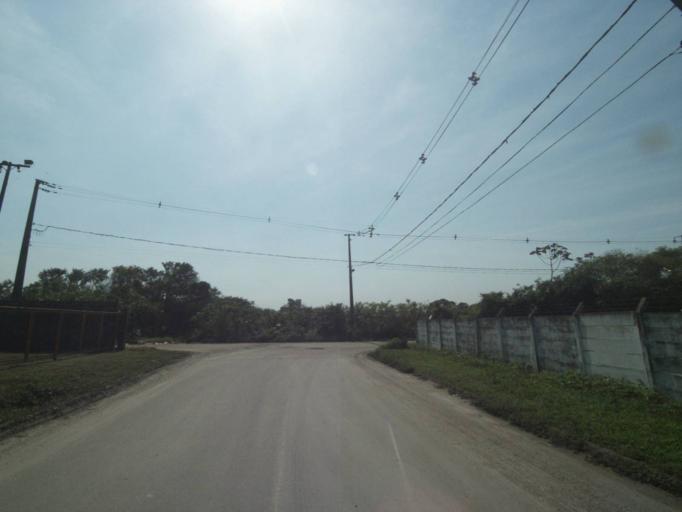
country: BR
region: Parana
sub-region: Paranagua
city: Paranagua
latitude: -25.5470
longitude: -48.5496
